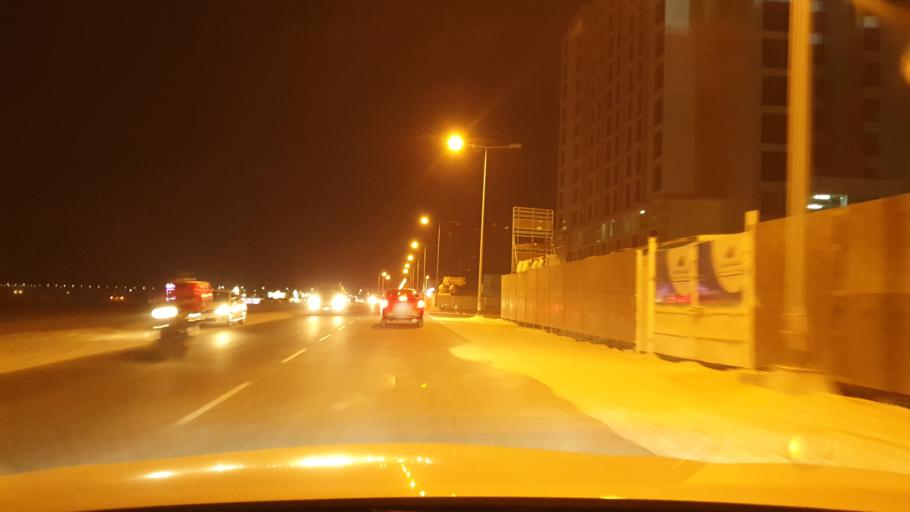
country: BH
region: Muharraq
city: Al Muharraq
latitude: 26.2642
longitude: 50.5945
